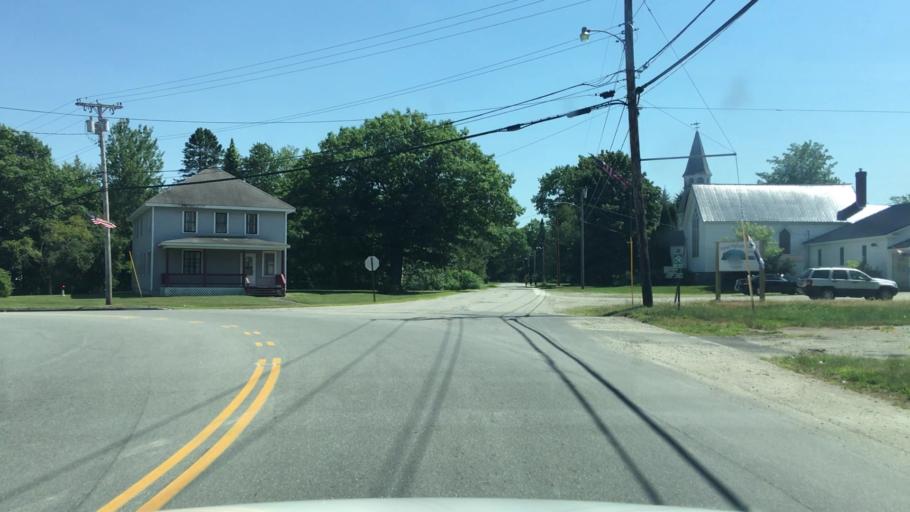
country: US
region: Maine
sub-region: Penobscot County
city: Howland
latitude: 45.2377
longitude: -68.6602
